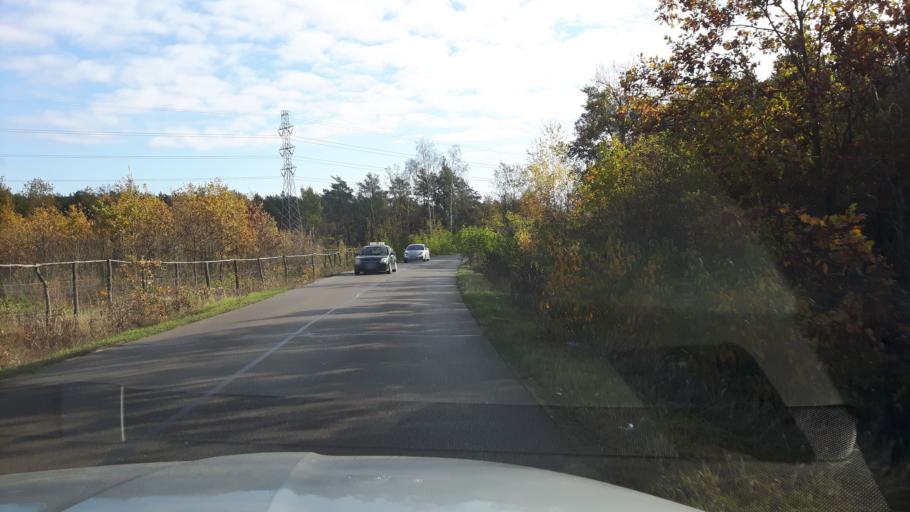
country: PL
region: Masovian Voivodeship
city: Zielonka
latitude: 52.2990
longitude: 21.1349
